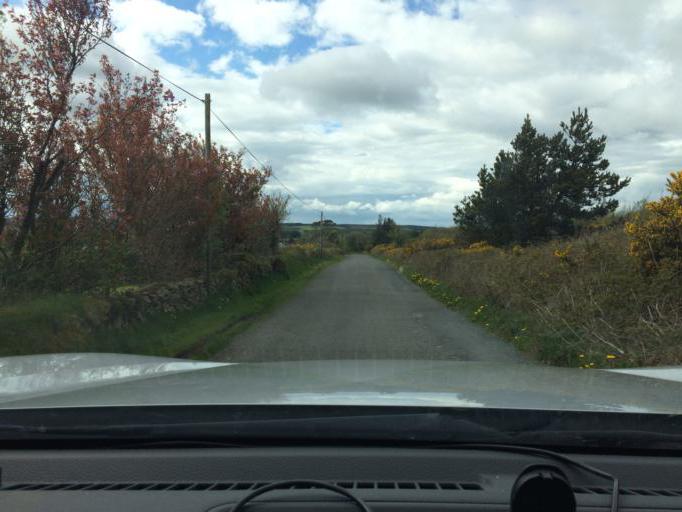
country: IE
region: Munster
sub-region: Waterford
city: Dungarvan
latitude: 52.0428
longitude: -7.6484
